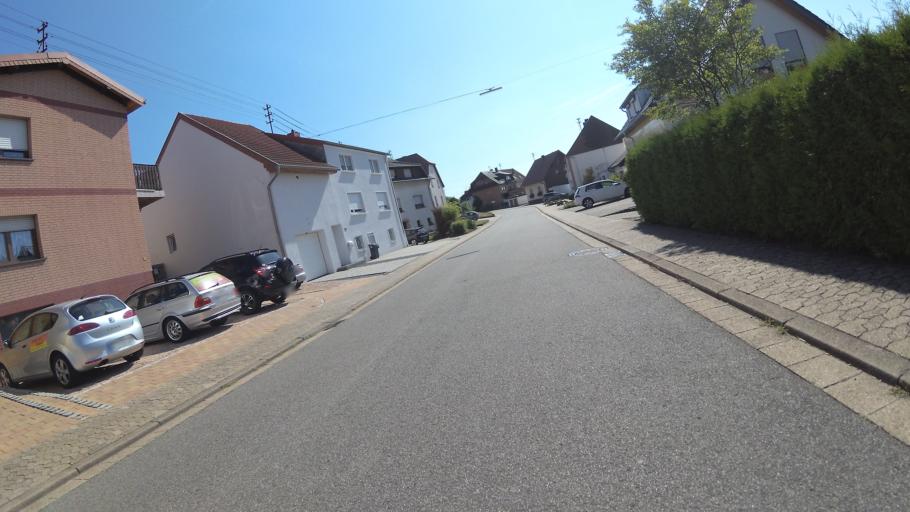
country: DE
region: Saarland
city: Eppelborn
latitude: 49.3734
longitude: 6.9865
